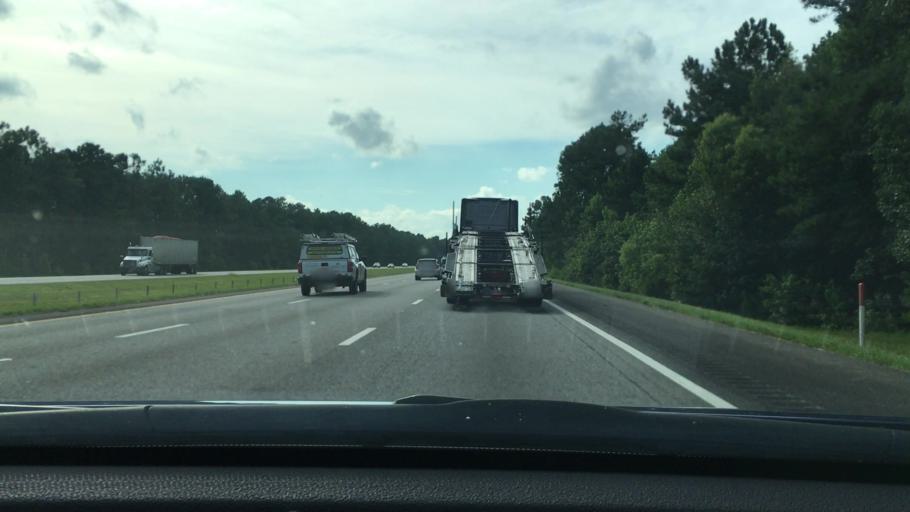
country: US
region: South Carolina
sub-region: Berkeley County
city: Sangaree
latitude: 33.0222
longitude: -80.1297
